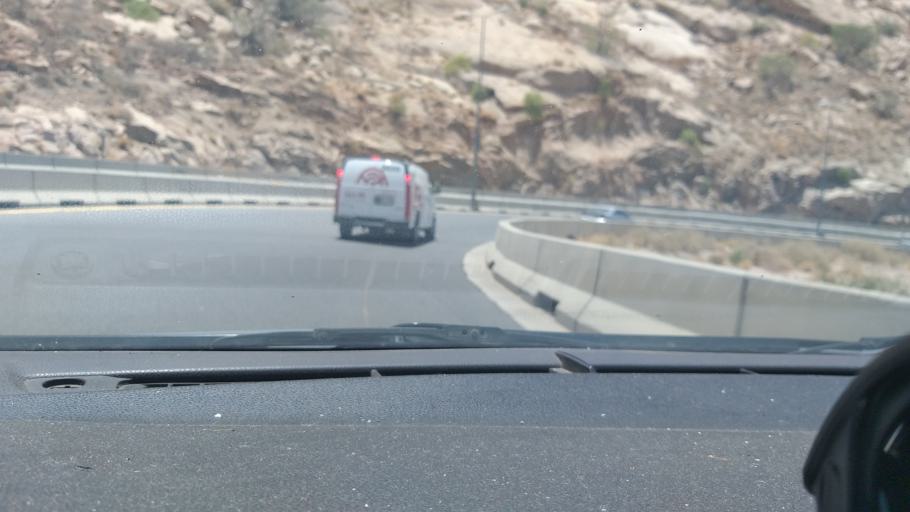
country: SA
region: Makkah
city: Al Hada
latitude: 21.3391
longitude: 40.2550
